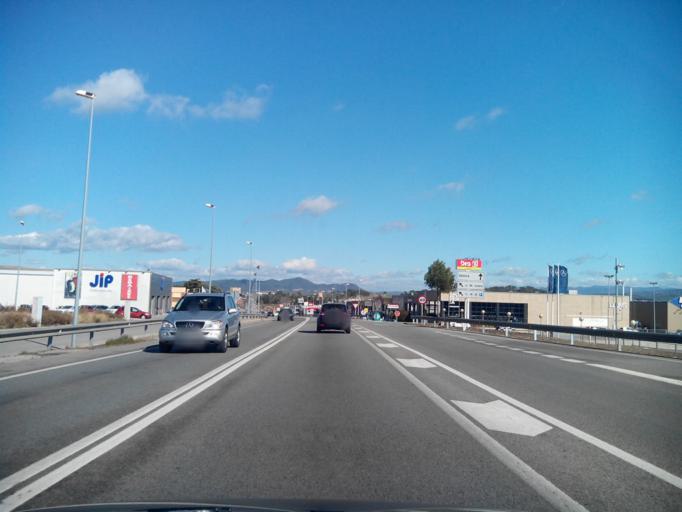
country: ES
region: Catalonia
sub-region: Provincia de Barcelona
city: Sant Fruitos de Bages
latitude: 41.7464
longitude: 1.8590
